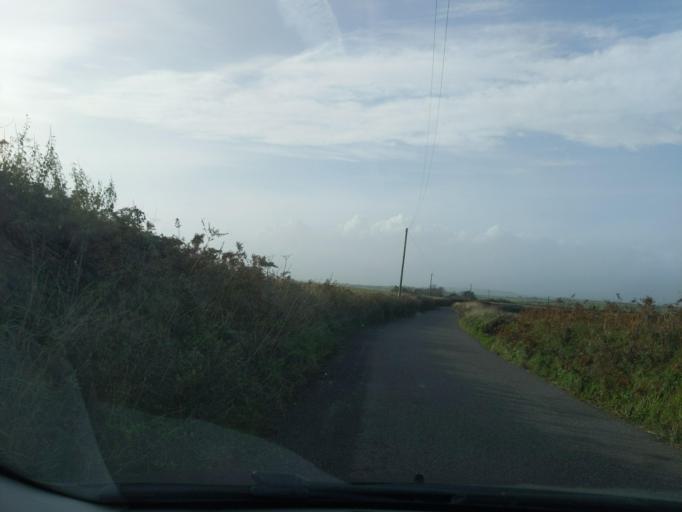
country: GB
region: England
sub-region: Cornwall
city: Pillaton
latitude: 50.3640
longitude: -4.3451
